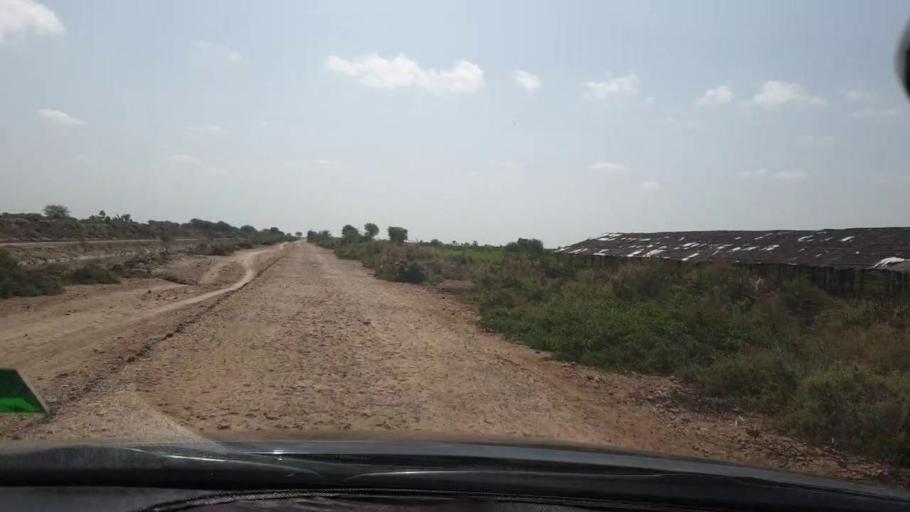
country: PK
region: Sindh
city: Tando Bago
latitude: 24.8447
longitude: 69.0391
